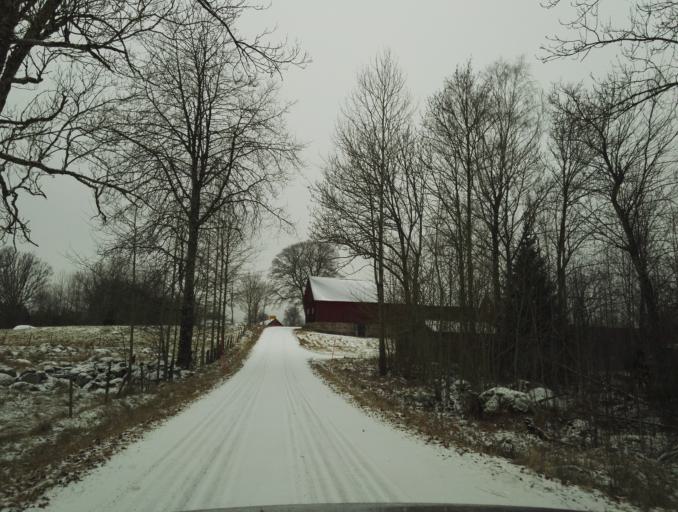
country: SE
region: Kronoberg
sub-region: Alvesta Kommun
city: Vislanda
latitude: 56.6821
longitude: 14.4317
